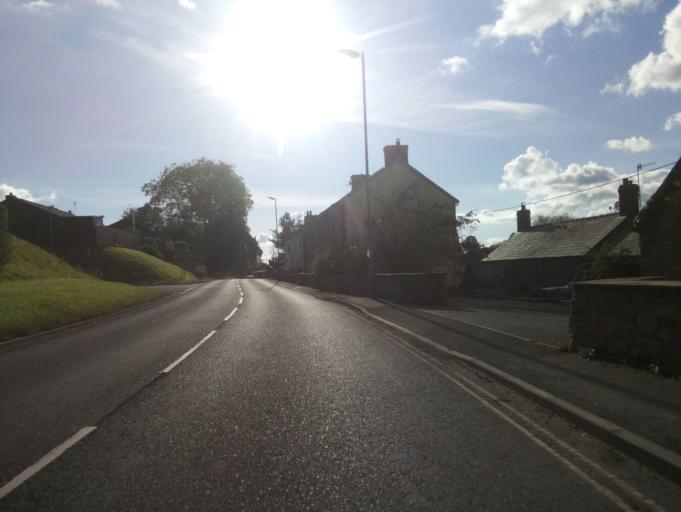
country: GB
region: Wales
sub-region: Sir Powys
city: Hay
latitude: 52.0468
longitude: -3.1939
